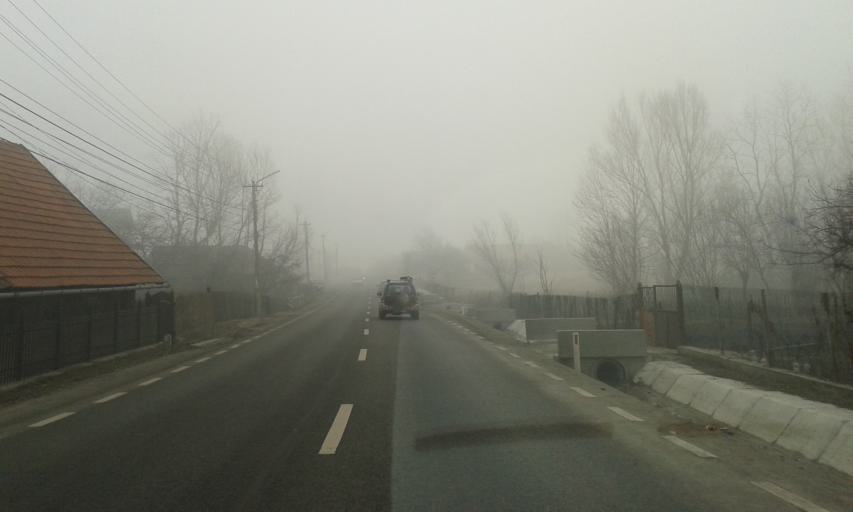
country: RO
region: Hunedoara
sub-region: Comuna Aninoasa
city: Iscroni
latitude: 45.3782
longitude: 23.3266
